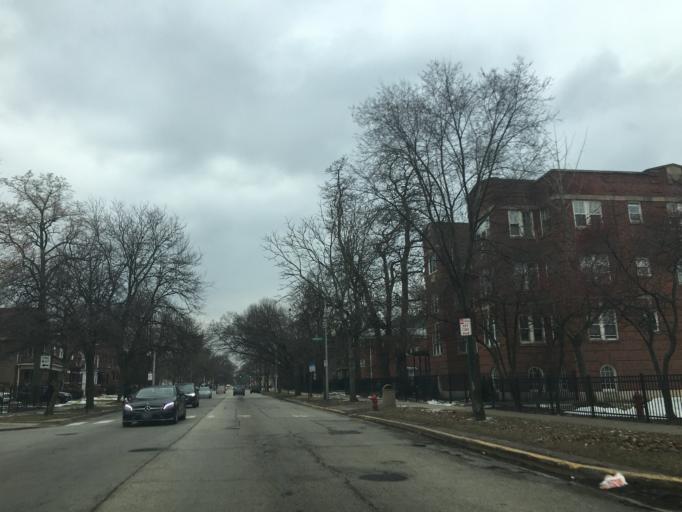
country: US
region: Illinois
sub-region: Cook County
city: Oak Park
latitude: 41.8842
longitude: -87.7748
